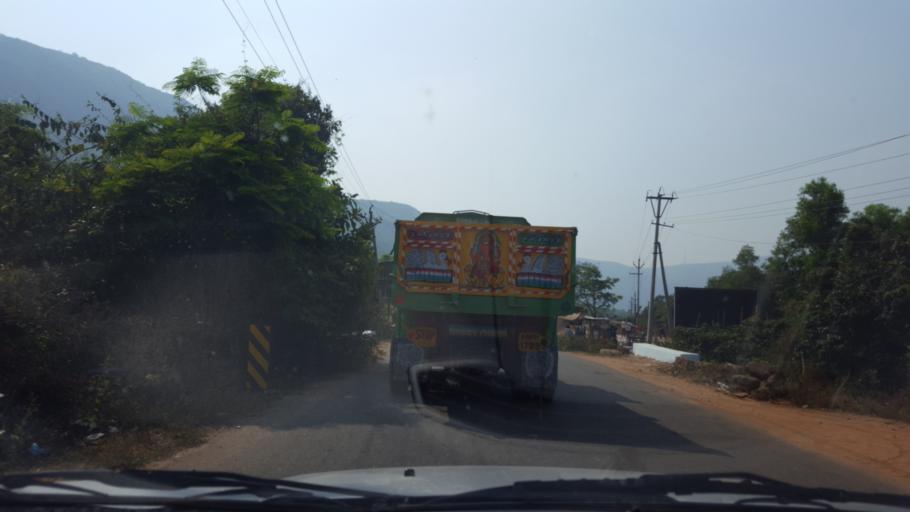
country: IN
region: Andhra Pradesh
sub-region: Vishakhapatnam
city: Vepagunta
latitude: 17.8005
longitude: 83.2562
